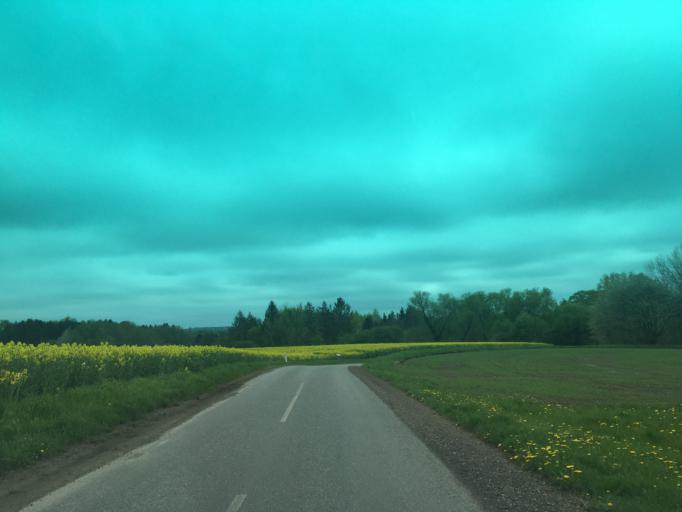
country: DK
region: Zealand
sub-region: Ringsted Kommune
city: Ringsted
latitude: 55.4145
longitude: 11.7065
